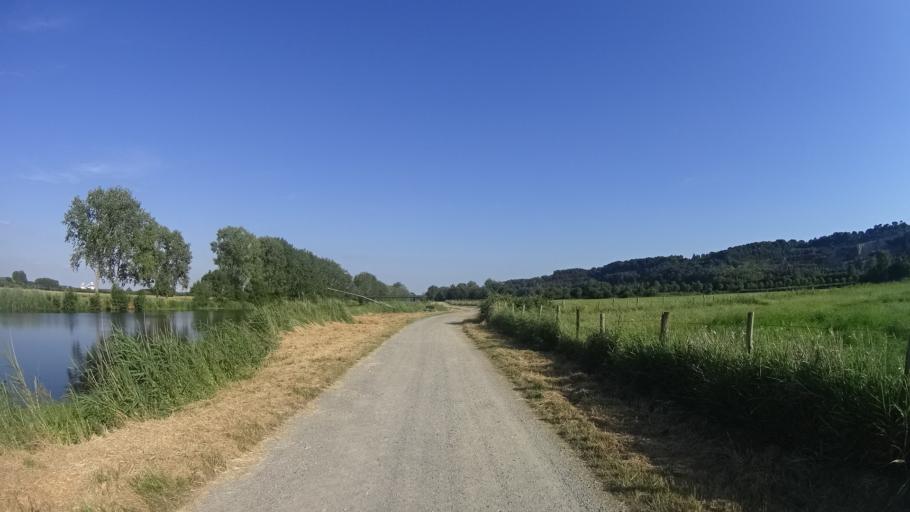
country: FR
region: Brittany
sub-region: Departement du Morbihan
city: Saint-Jean-la-Poterie
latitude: 47.6441
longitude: -2.1107
